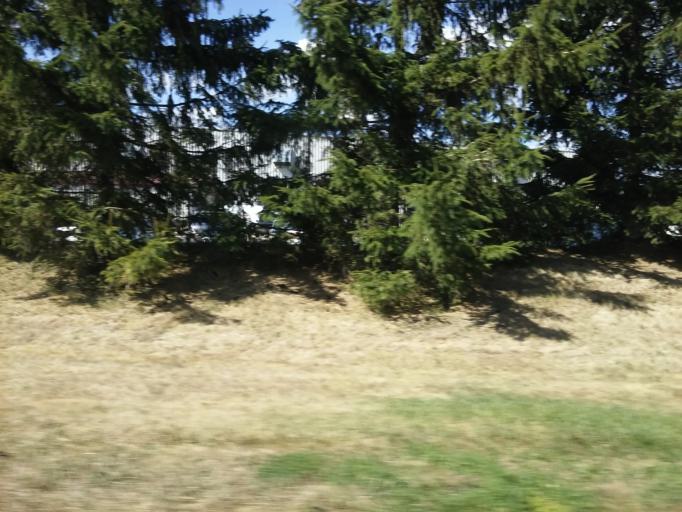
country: US
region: Ohio
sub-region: Wood County
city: Bowling Green
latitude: 41.3567
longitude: -83.6442
